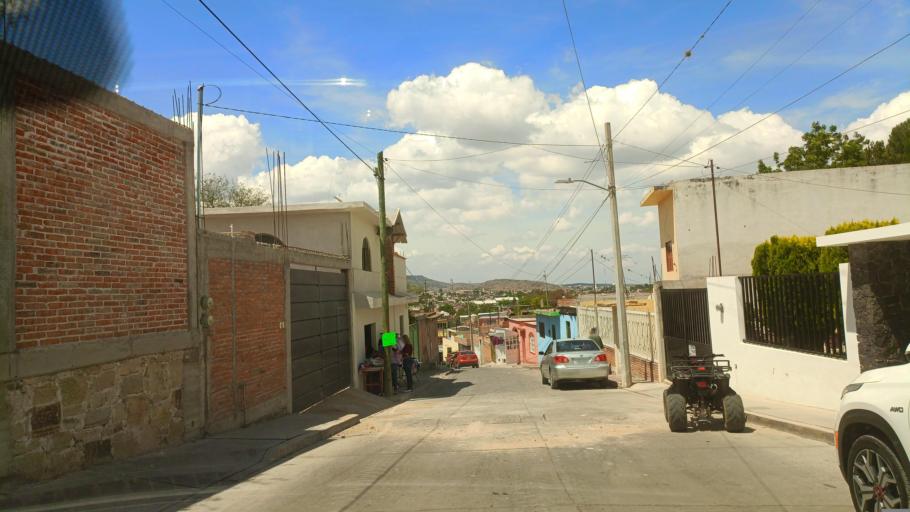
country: MX
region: Guanajuato
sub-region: San Luis de la Paz
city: San Luis de la Paz
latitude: 21.3051
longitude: -100.5140
